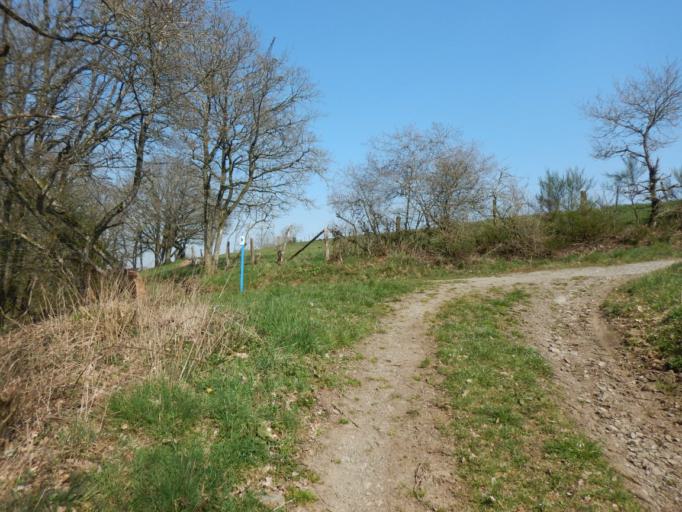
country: LU
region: Diekirch
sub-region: Canton de Diekirch
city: Bourscheid
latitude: 49.9428
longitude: 6.0692
